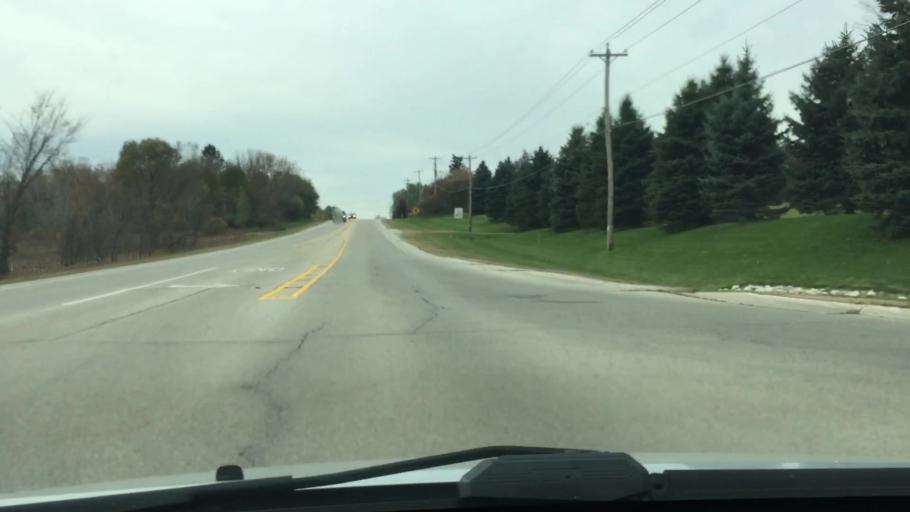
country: US
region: Wisconsin
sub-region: Waukesha County
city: Mukwonago
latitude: 42.8787
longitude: -88.2999
